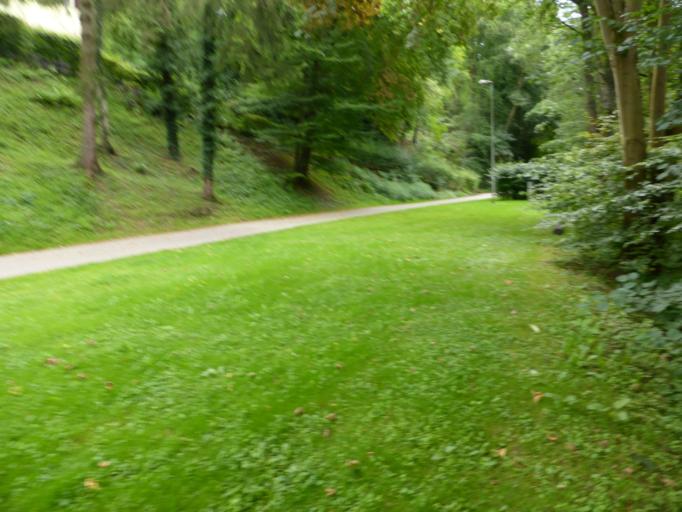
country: LU
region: Diekirch
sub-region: Canton de Diekirch
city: Ettelbruck
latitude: 49.8455
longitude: 6.1067
